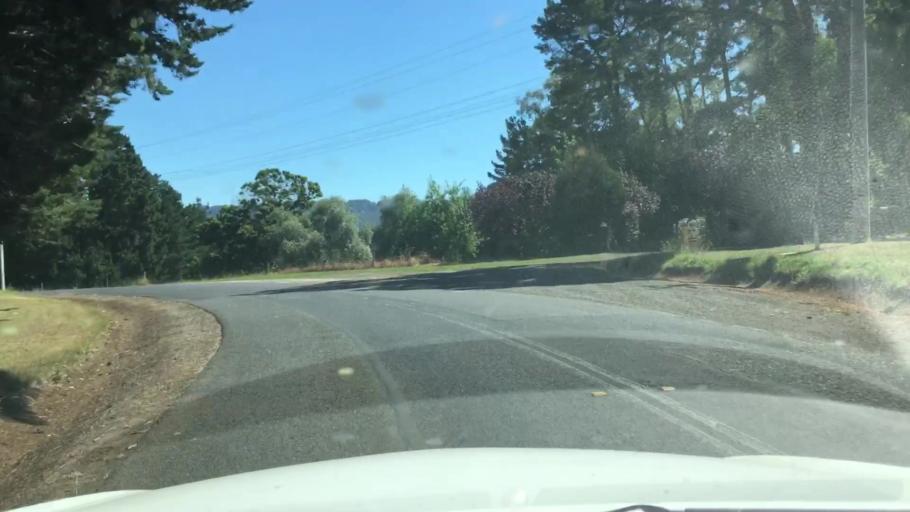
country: AU
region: Victoria
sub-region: Yarra Ranges
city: Mount Evelyn
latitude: -37.8130
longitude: 145.4235
